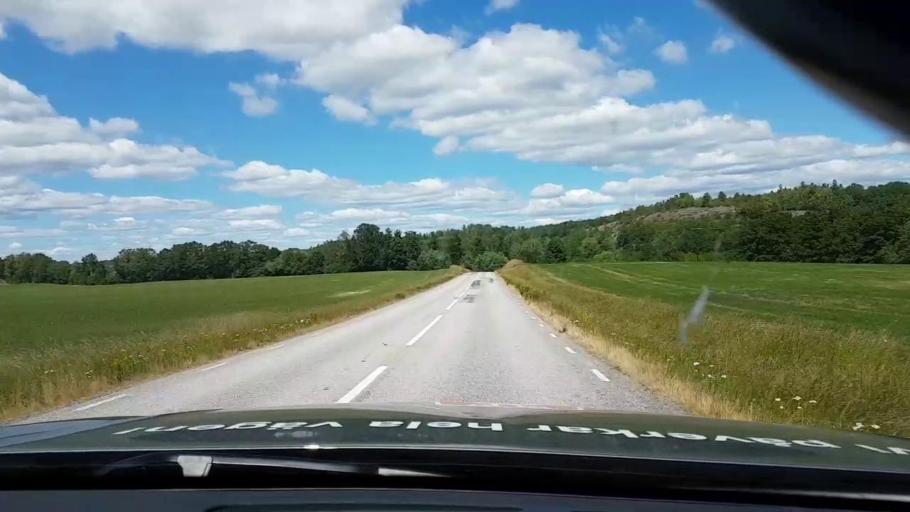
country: SE
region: Kalmar
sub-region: Vasterviks Kommun
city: Overum
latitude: 58.0517
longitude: 16.4060
